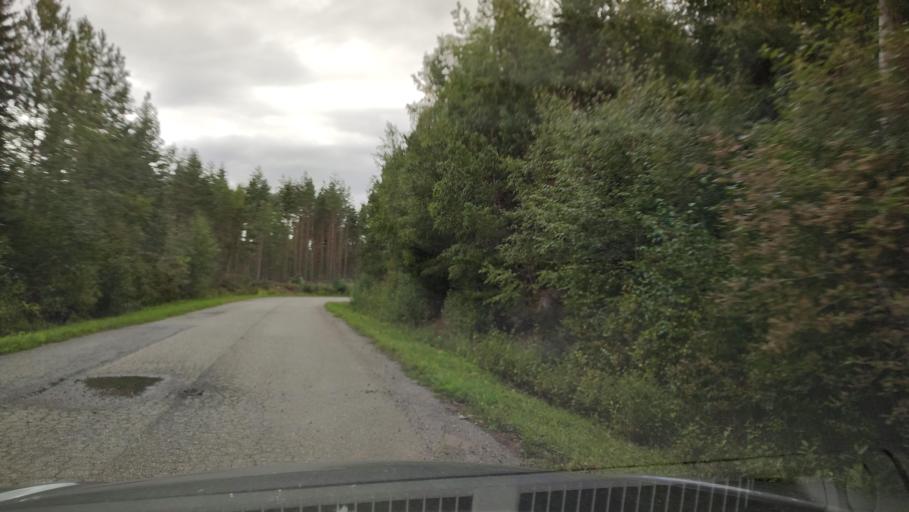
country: FI
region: Ostrobothnia
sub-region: Sydosterbotten
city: Kristinestad
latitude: 62.2538
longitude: 21.3350
